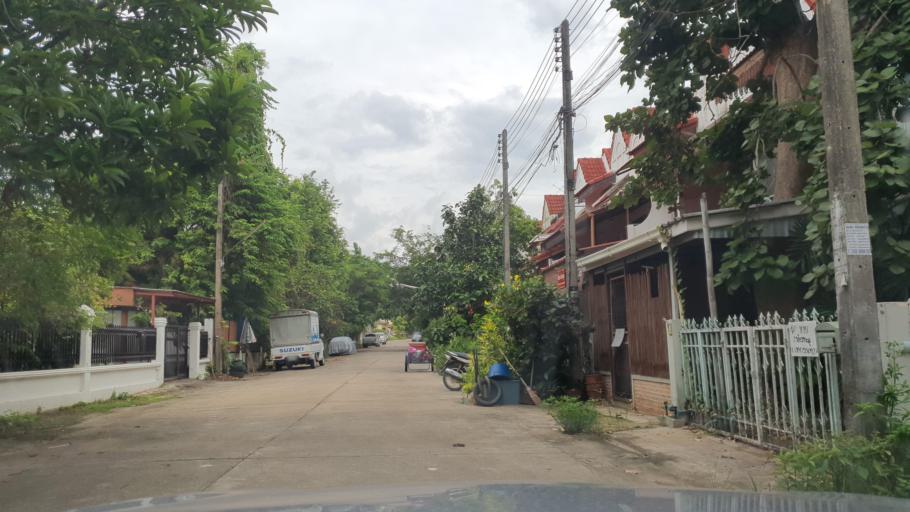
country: TH
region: Chiang Mai
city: Chiang Mai
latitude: 18.7763
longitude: 98.9517
